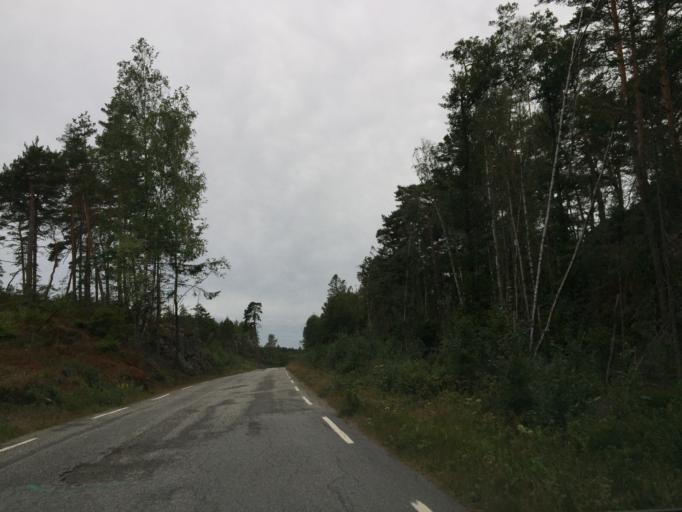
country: NO
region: Ostfold
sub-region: Hvaler
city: Skjaerhalden
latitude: 59.0784
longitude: 11.0147
